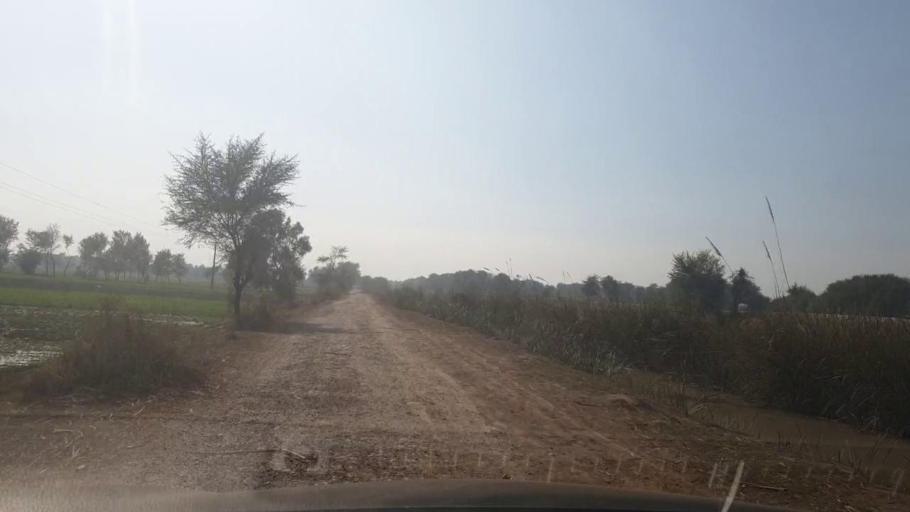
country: PK
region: Sindh
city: Ubauro
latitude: 28.1426
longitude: 69.6868
